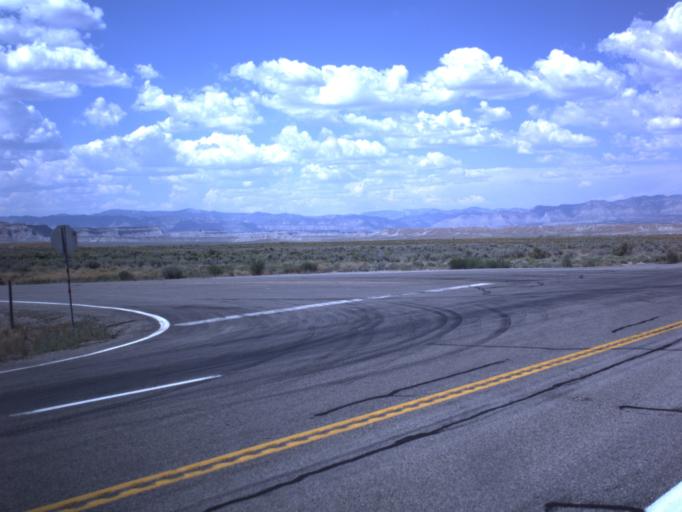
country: US
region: Utah
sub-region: Carbon County
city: Price
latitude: 39.4930
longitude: -110.8457
